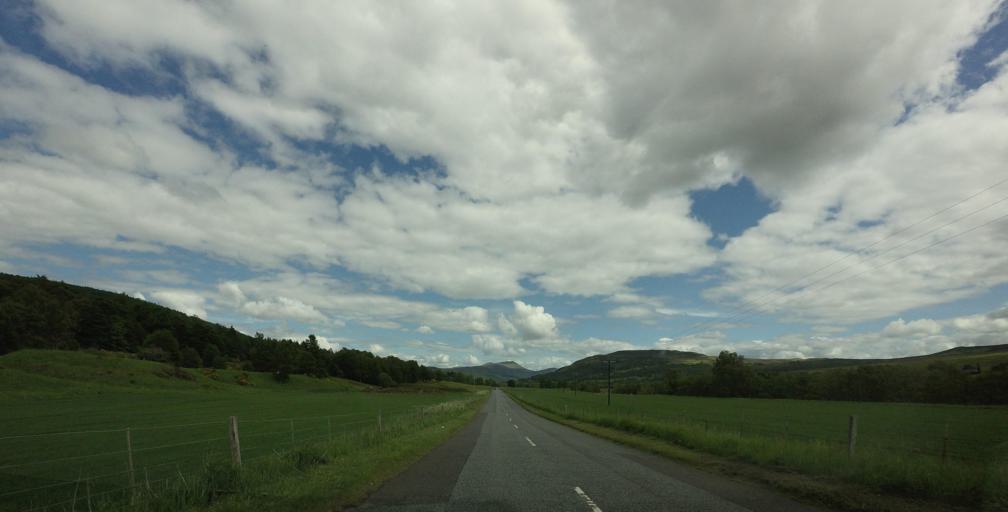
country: GB
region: Scotland
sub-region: Perth and Kinross
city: Aberfeldy
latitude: 56.7711
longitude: -3.9229
